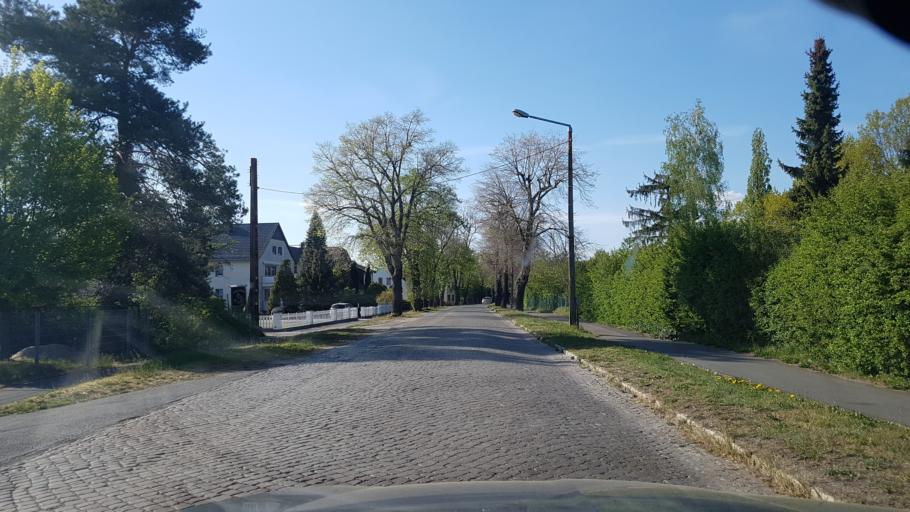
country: DE
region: Brandenburg
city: Elsterwerda
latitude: 51.4663
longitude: 13.5163
